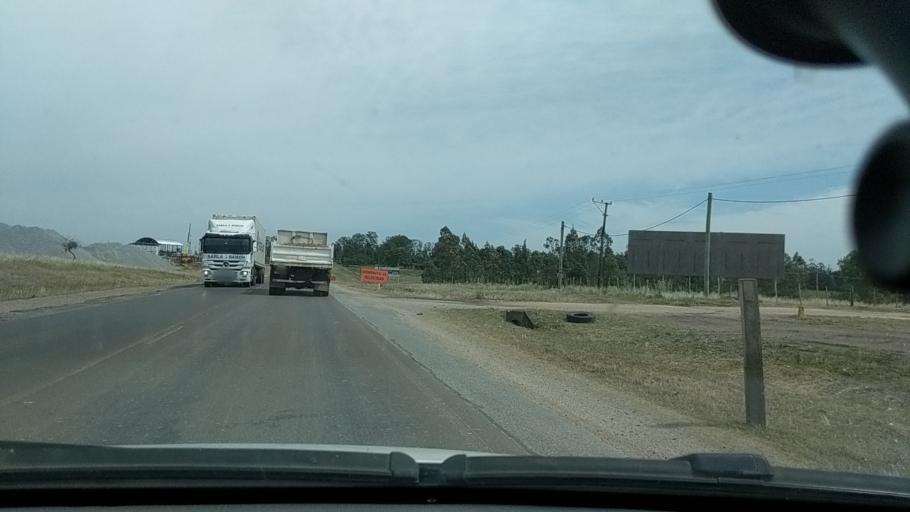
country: UY
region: Durazno
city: Durazno
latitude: -33.4227
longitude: -56.5017
